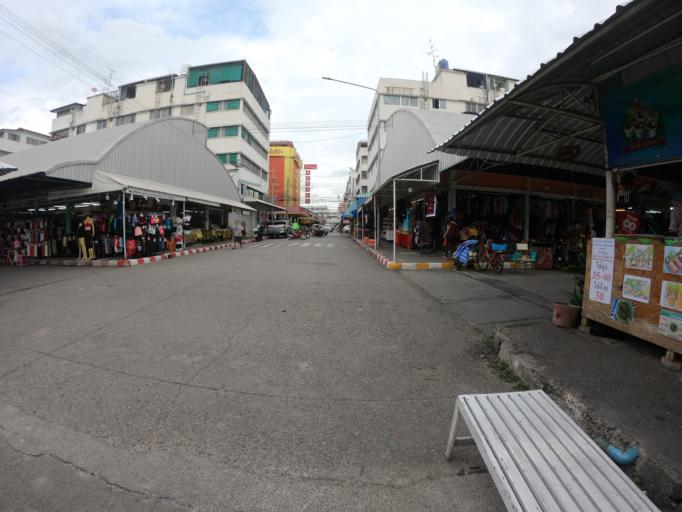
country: TH
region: Bangkok
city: Bang Na
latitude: 13.6710
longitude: 100.6824
